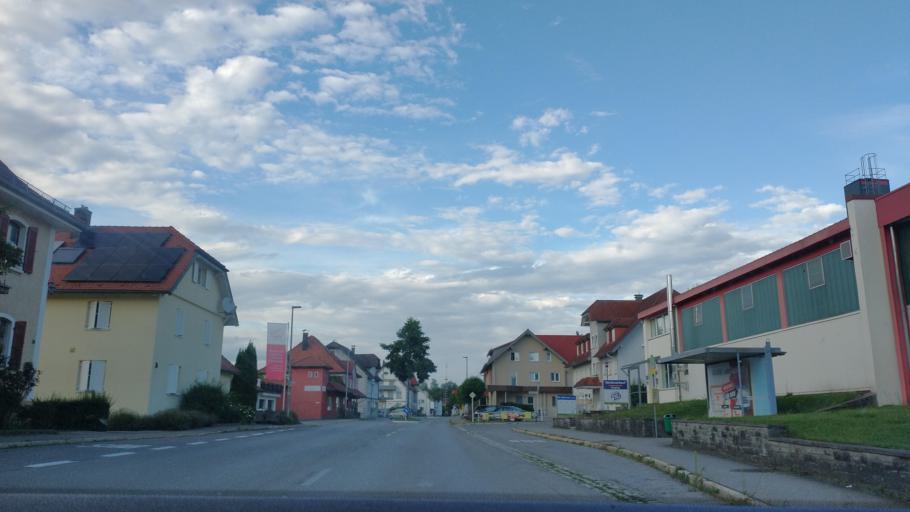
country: DE
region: Bavaria
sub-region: Swabia
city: Hergensweiler
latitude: 47.6390
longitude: 9.7597
